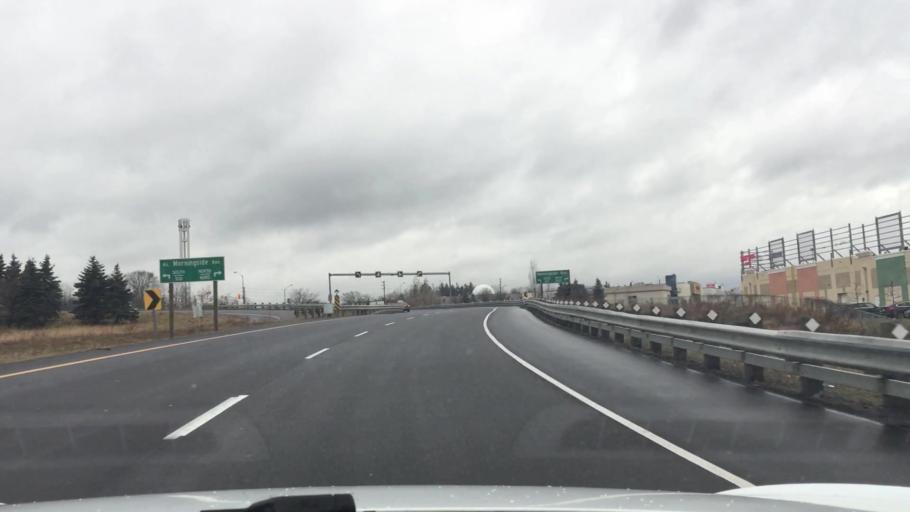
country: CA
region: Ontario
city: Scarborough
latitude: 43.7976
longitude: -79.1954
